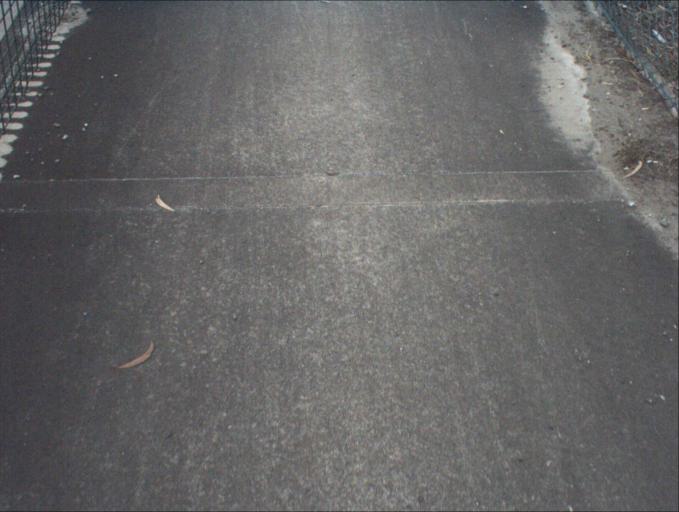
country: AU
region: Queensland
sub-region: Logan
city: Beenleigh
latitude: -27.6769
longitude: 153.1853
